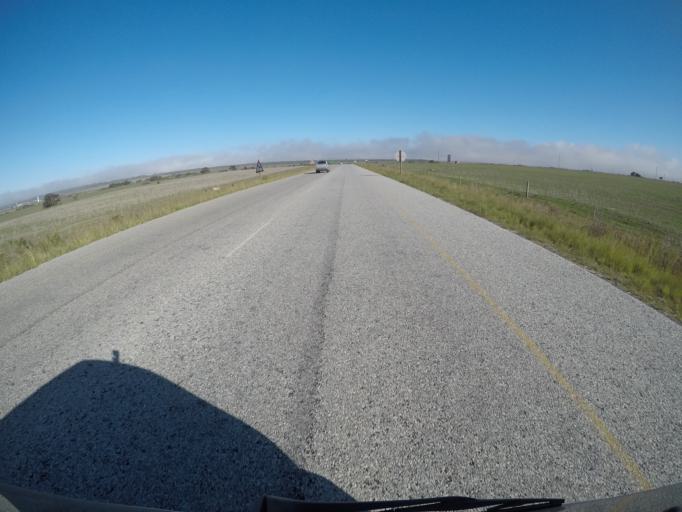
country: ZA
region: Western Cape
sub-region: Eden District Municipality
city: Mossel Bay
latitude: -34.1776
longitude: 22.0164
